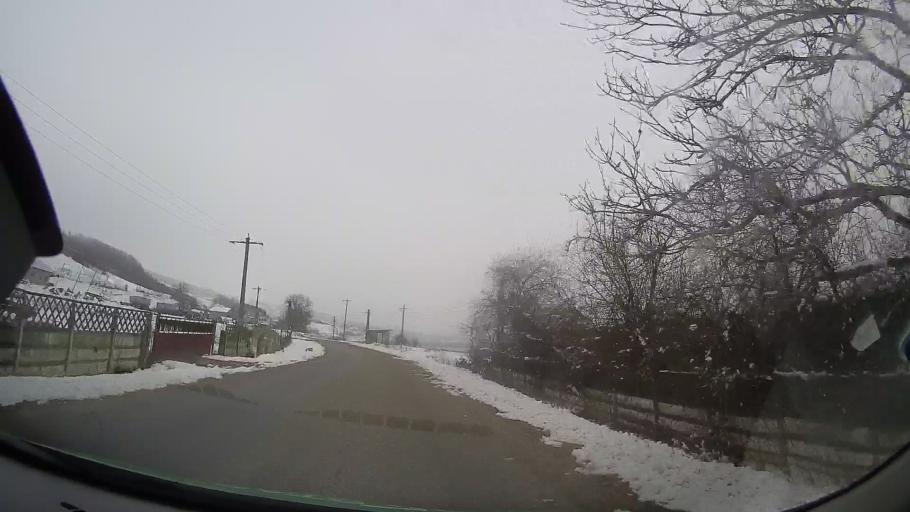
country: RO
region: Bacau
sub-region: Comuna Vultureni
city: Vultureni
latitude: 46.3690
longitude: 27.2827
